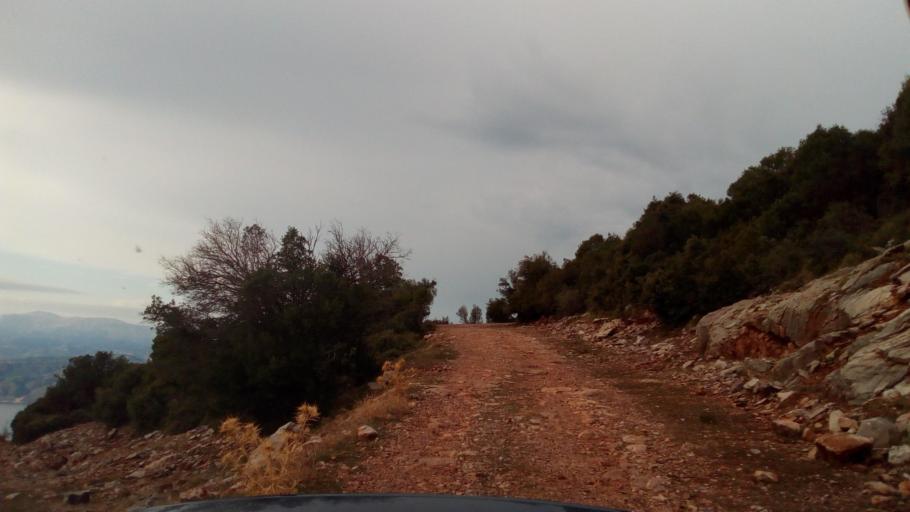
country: GR
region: West Greece
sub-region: Nomos Achaias
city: Kamarai
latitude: 38.4087
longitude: 22.0453
